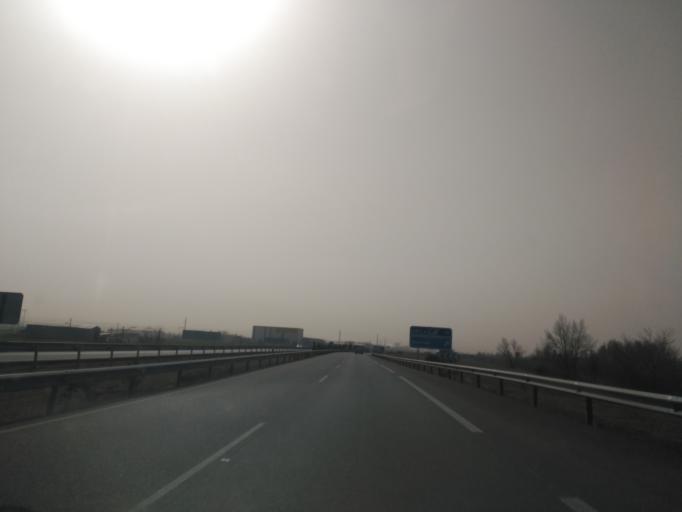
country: ES
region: Castille and Leon
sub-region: Provincia de Palencia
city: Duenas
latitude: 41.8617
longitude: -4.5478
